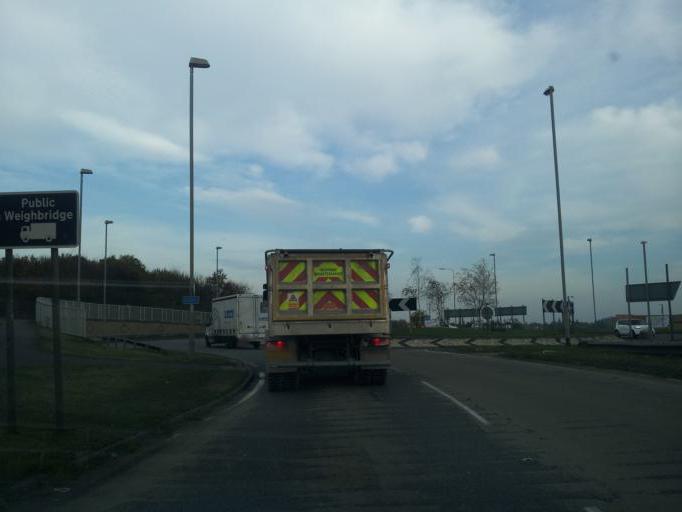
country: GB
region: England
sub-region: Cambridgeshire
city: Duxford
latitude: 52.1010
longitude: 0.1432
